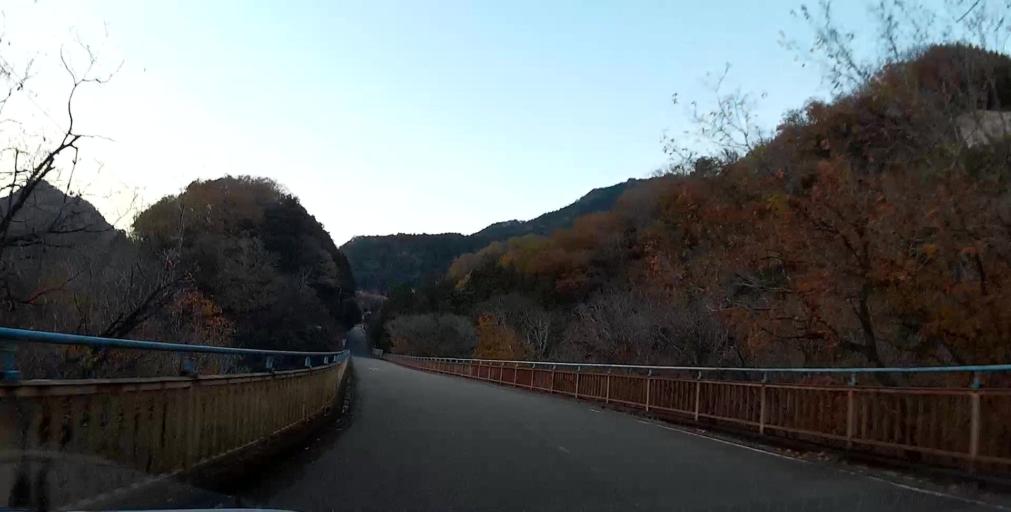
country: JP
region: Yamanashi
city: Uenohara
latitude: 35.5679
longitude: 139.2052
